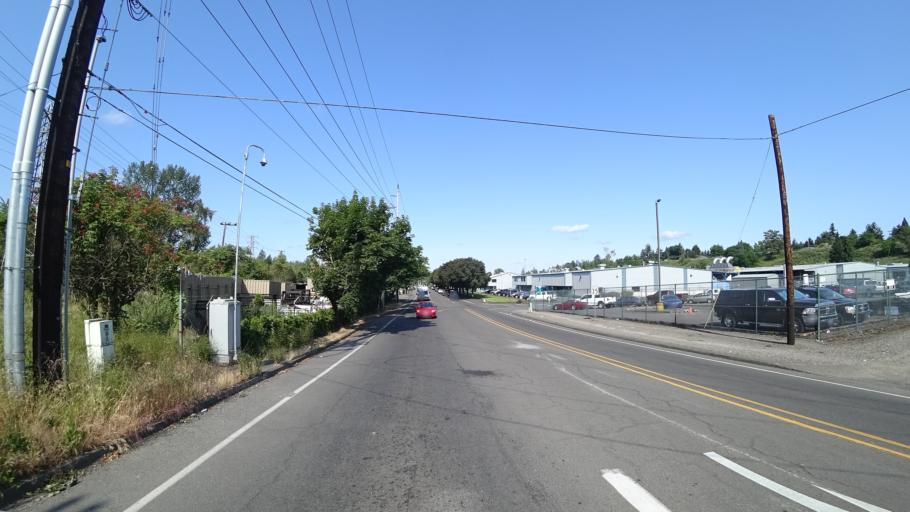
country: US
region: Oregon
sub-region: Multnomah County
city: Lents
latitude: 45.4559
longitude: -122.5934
